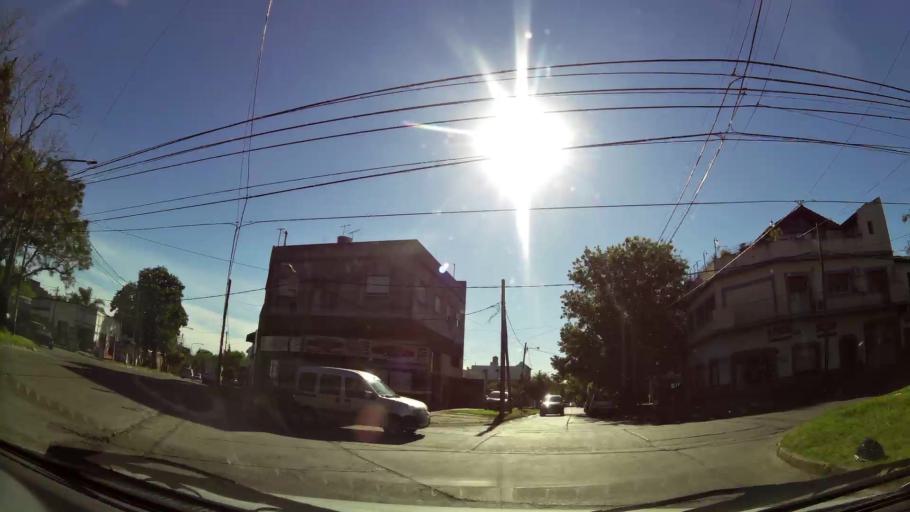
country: AR
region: Buenos Aires
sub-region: Partido de Lomas de Zamora
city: Lomas de Zamora
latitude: -34.7699
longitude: -58.4135
